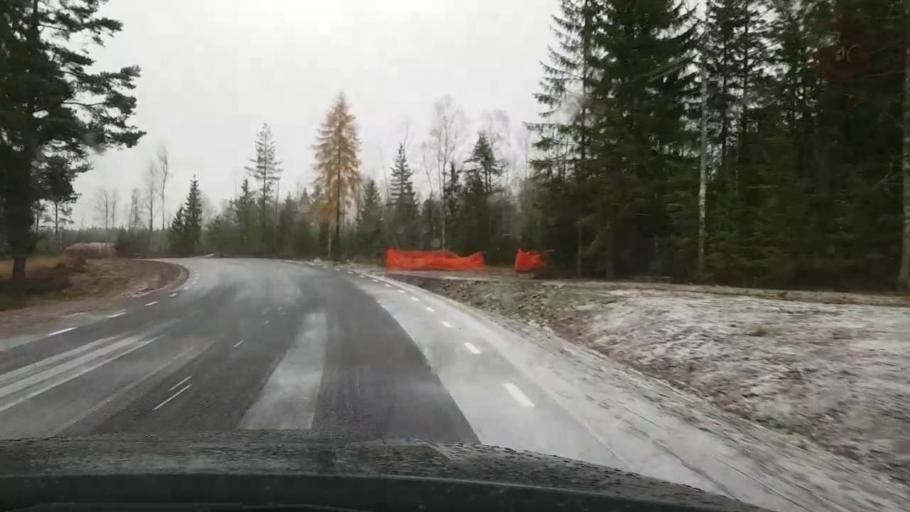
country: SE
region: Vaestra Goetaland
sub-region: Karlsborgs Kommun
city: Karlsborg
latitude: 58.7079
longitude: 14.5036
